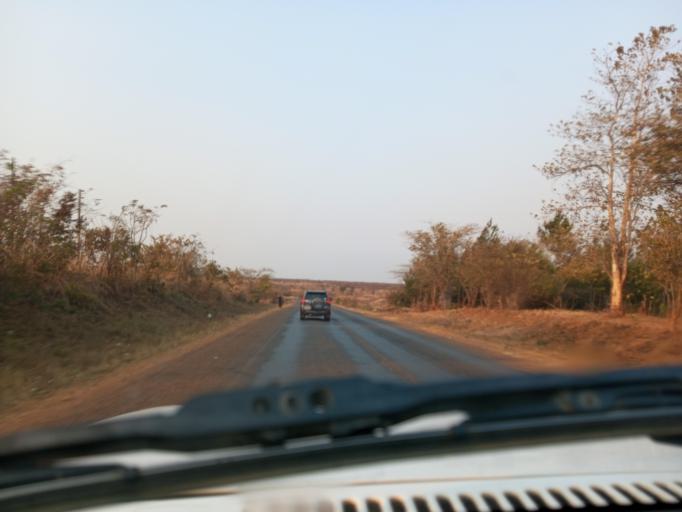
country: ZM
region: Northern
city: Mpika
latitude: -11.8970
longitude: 31.4155
